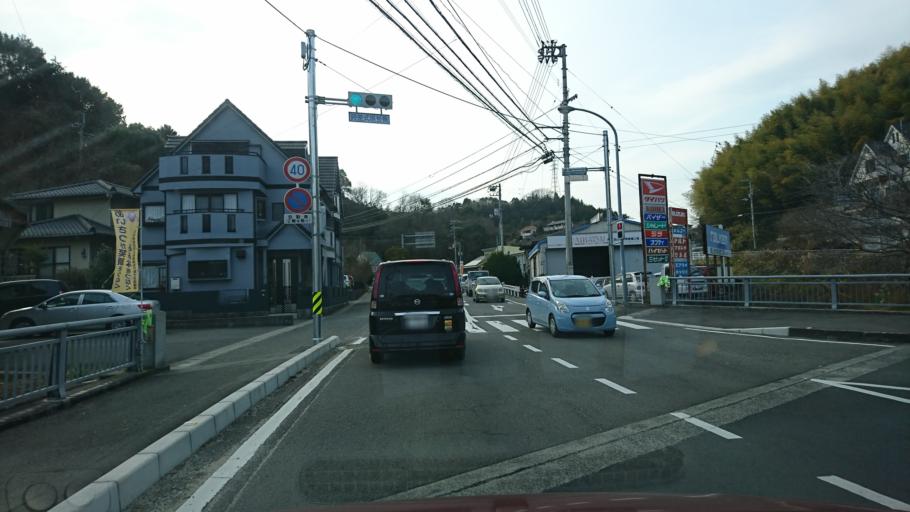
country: JP
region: Ehime
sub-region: Shikoku-chuo Shi
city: Matsuyama
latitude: 33.8759
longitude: 132.7967
